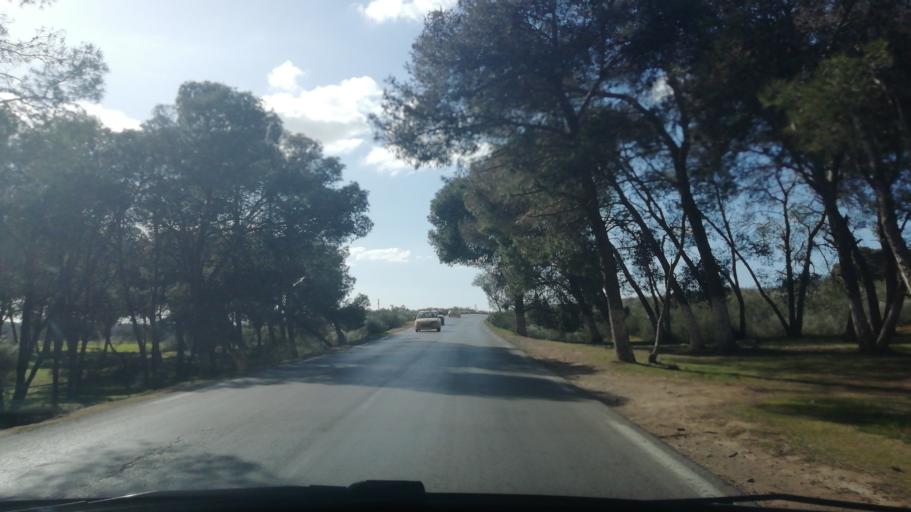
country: DZ
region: Mostaganem
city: Mostaganem
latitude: 35.9551
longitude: 0.2413
